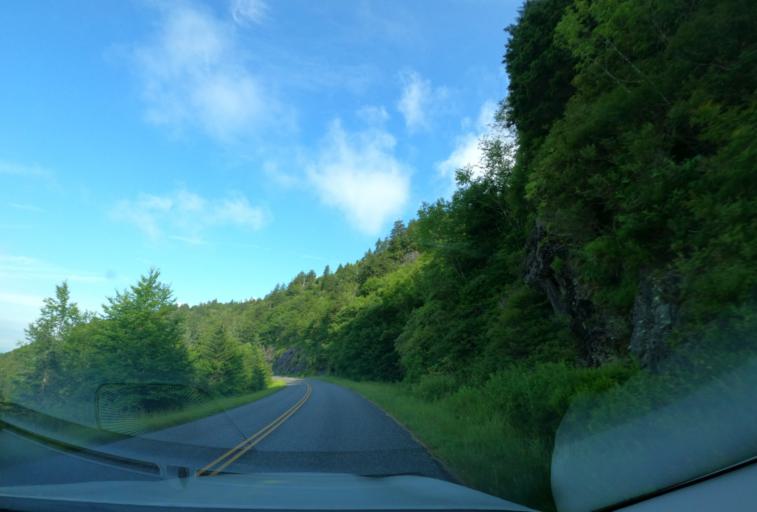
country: US
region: North Carolina
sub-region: Haywood County
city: Hazelwood
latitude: 35.3021
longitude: -82.9348
